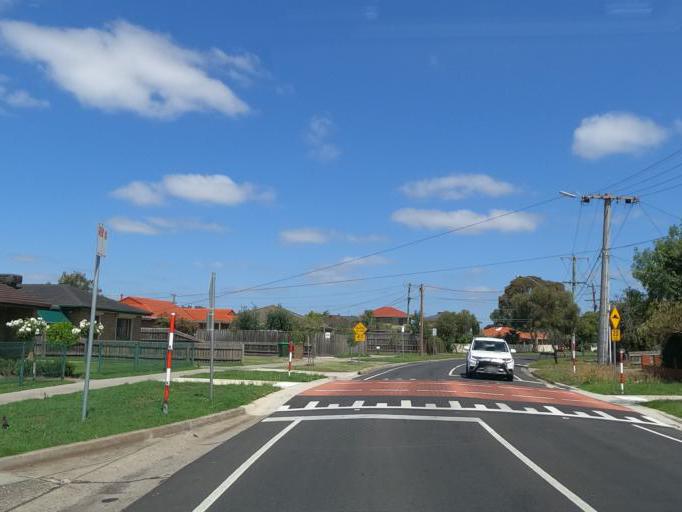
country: AU
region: Victoria
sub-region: Hume
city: Gladstone Park
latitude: -37.6921
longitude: 144.8895
